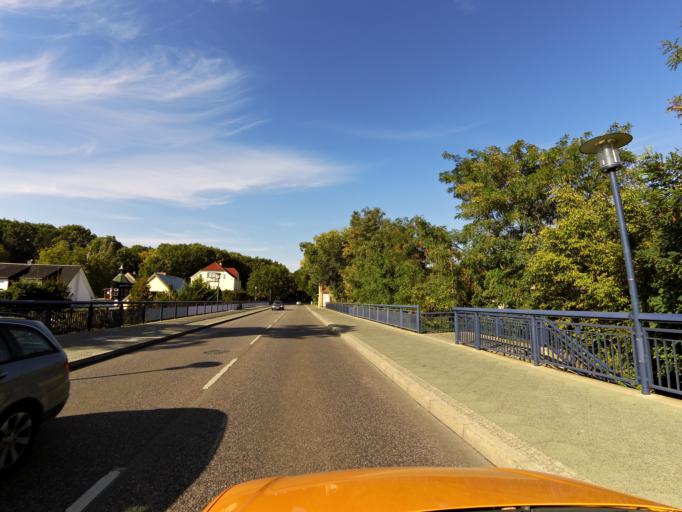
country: DE
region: Brandenburg
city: Potsdam
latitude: 52.4416
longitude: 13.0482
